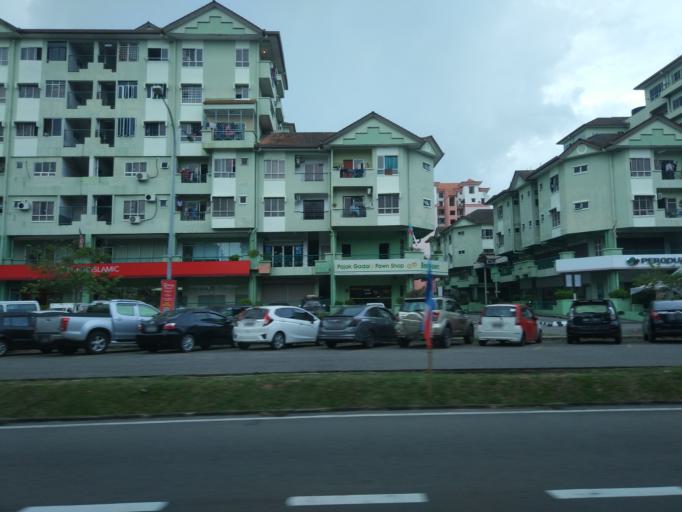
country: MY
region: Sabah
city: Kota Kinabalu
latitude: 5.9746
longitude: 116.0702
